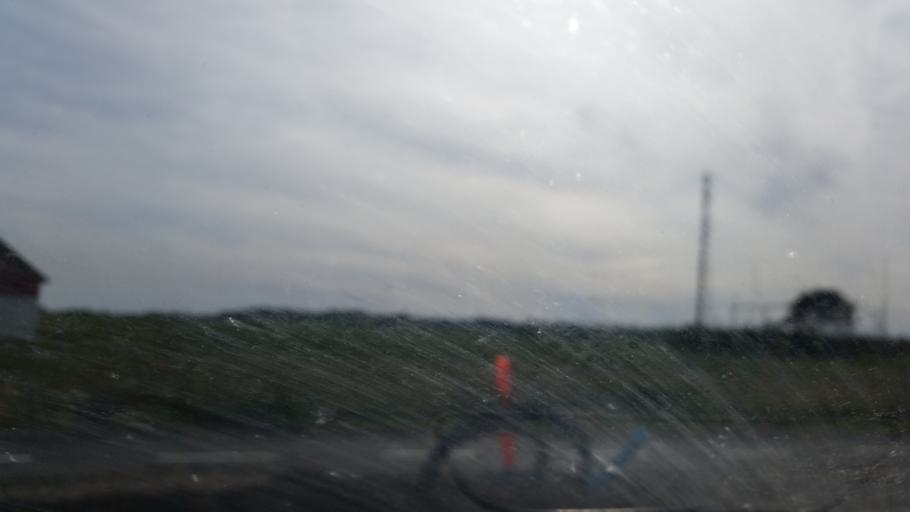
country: DK
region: Central Jutland
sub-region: Samso Kommune
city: Tranebjerg
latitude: 55.9448
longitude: 10.5660
